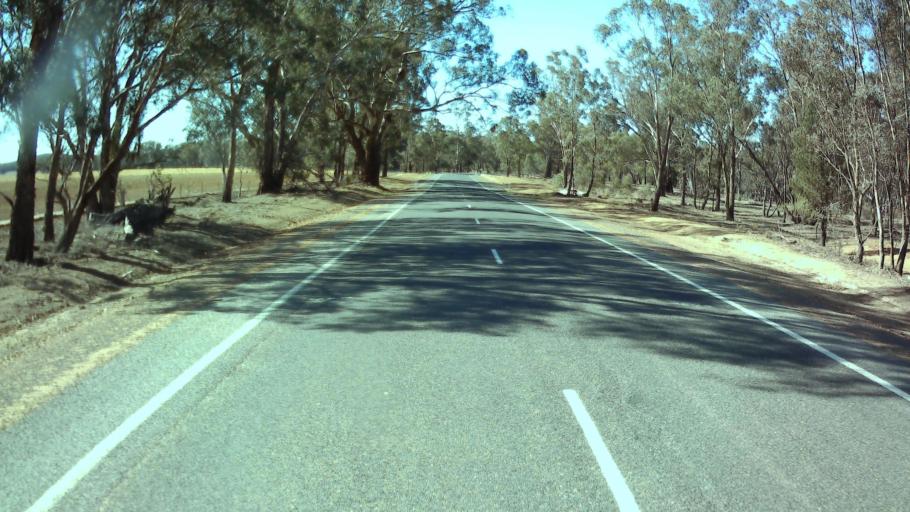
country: AU
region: New South Wales
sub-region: Weddin
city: Grenfell
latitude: -33.7662
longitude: 148.0825
